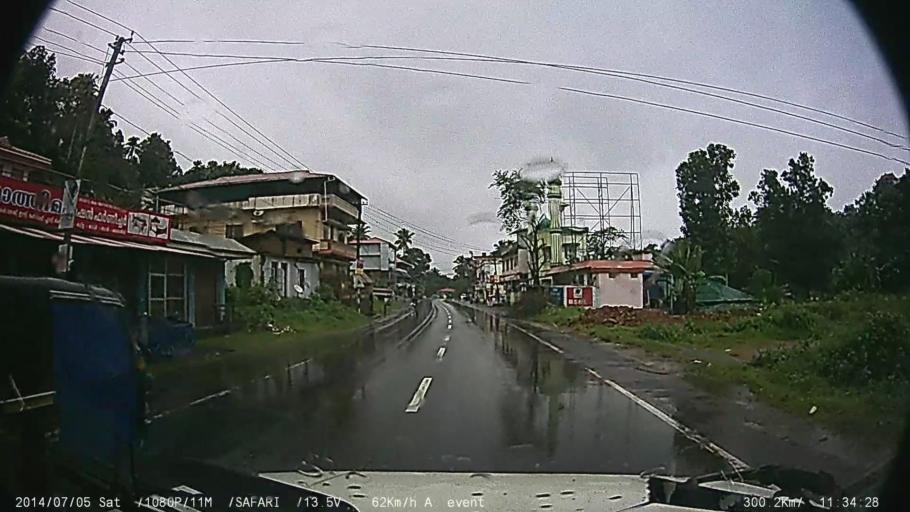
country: IN
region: Kerala
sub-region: Ernakulam
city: Muvattupula
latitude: 9.9752
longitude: 76.5943
